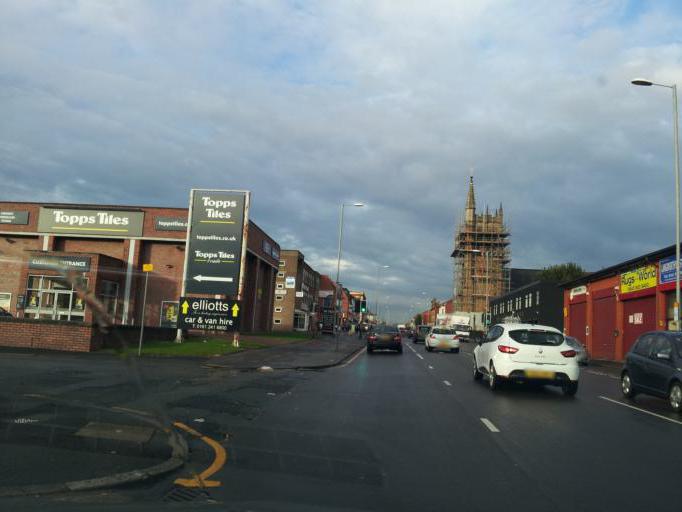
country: GB
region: England
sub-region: Manchester
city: Cheetham Hill
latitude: 53.4911
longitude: -2.2411
